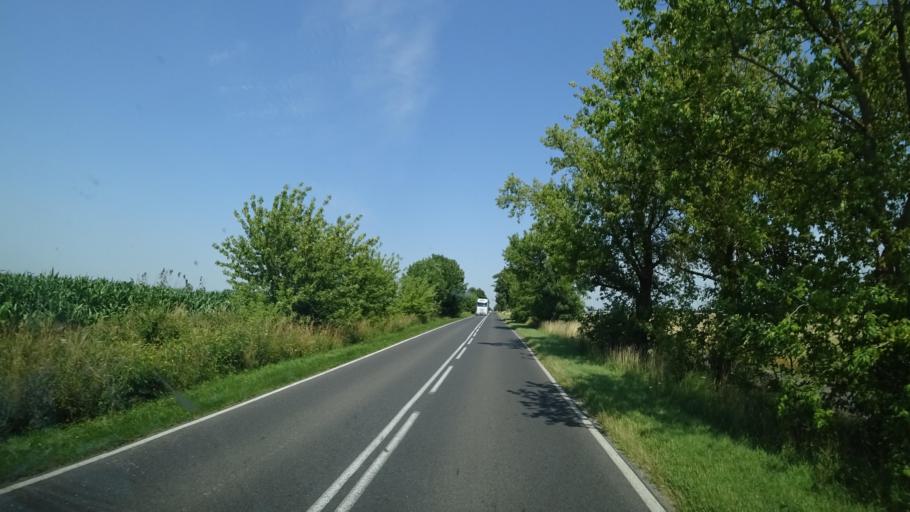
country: PL
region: Pomeranian Voivodeship
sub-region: Powiat chojnicki
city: Brusy
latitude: 53.9091
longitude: 17.7308
